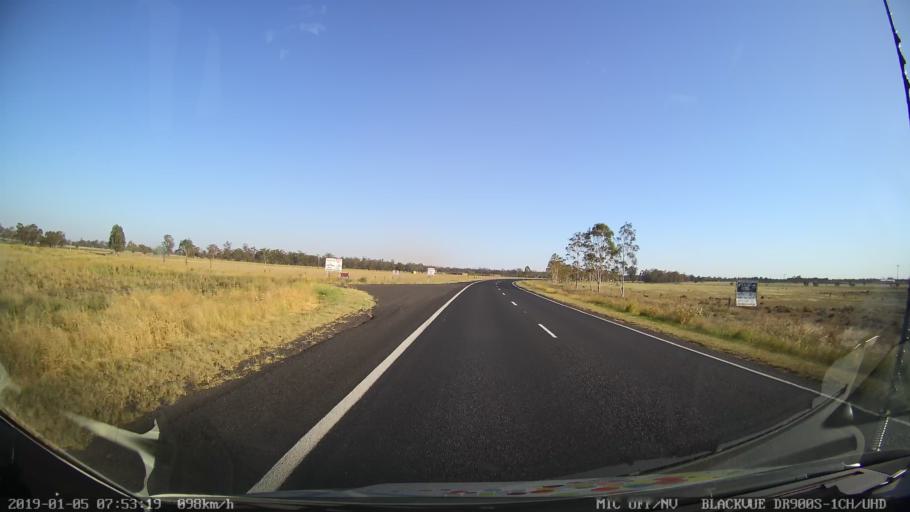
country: AU
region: New South Wales
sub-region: Gilgandra
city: Gilgandra
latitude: -31.7458
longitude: 148.6413
